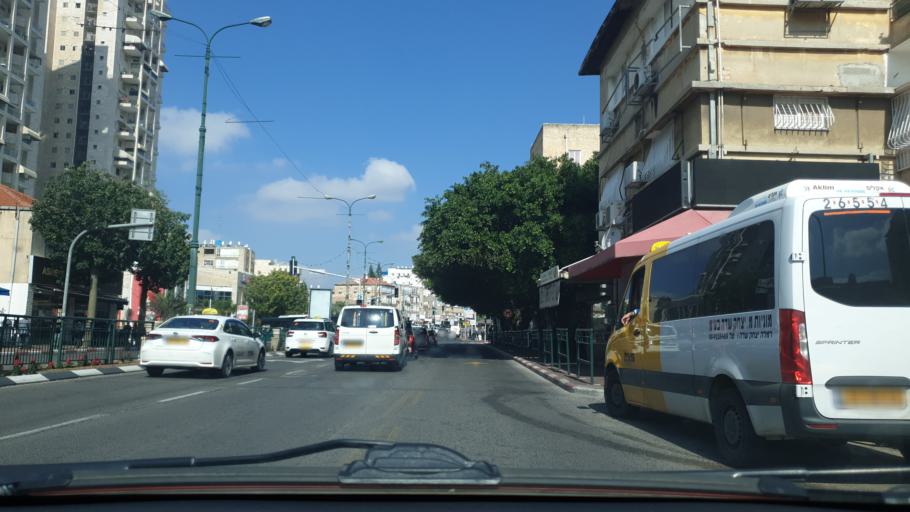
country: IL
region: Central District
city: Rishon LeZiyyon
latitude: 31.9651
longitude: 34.8030
